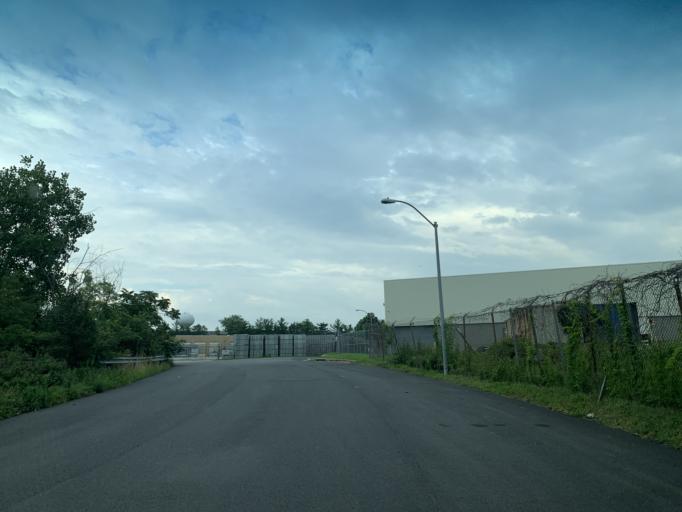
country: US
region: Maryland
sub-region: Baltimore County
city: Rosedale
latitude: 39.2953
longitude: -76.5298
